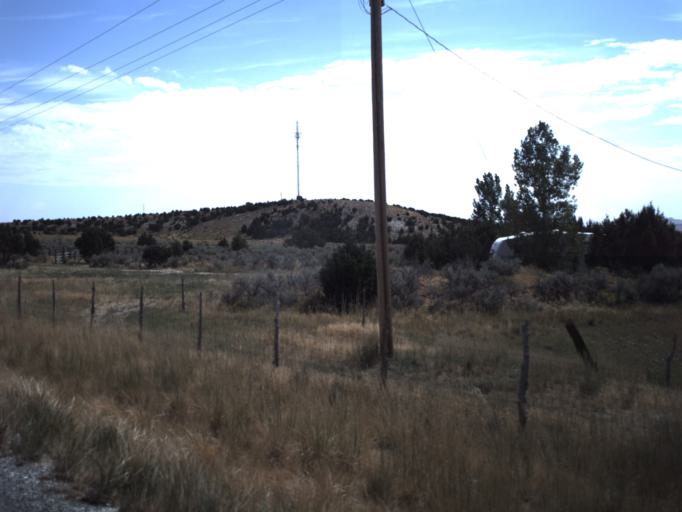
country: US
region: Idaho
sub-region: Cassia County
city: Burley
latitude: 41.8171
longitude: -113.3095
